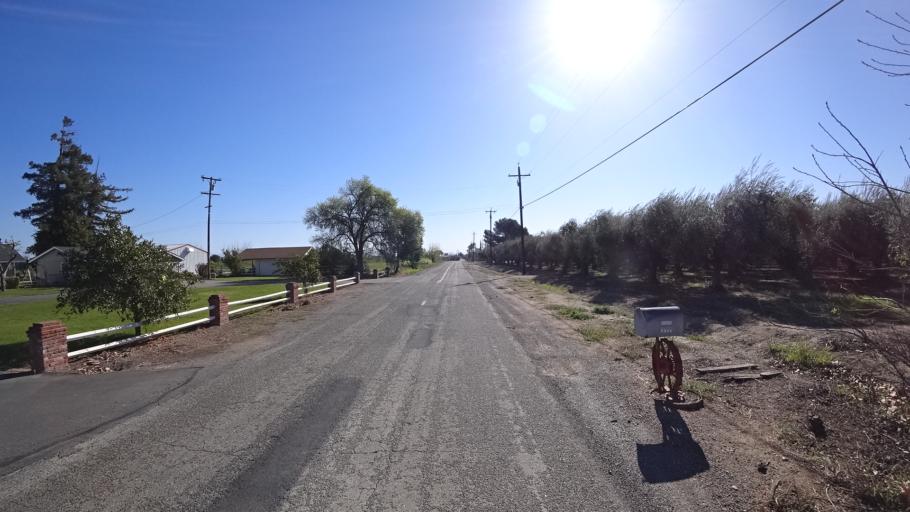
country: US
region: California
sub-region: Glenn County
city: Orland
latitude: 39.7476
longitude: -122.2187
